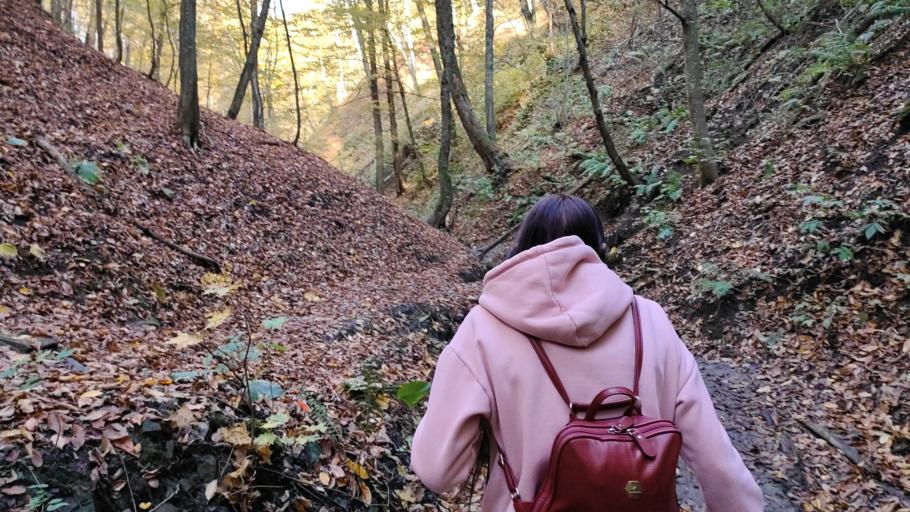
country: RU
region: Krasnodarskiy
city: Goryachiy Klyuch
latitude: 44.6026
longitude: 39.1154
